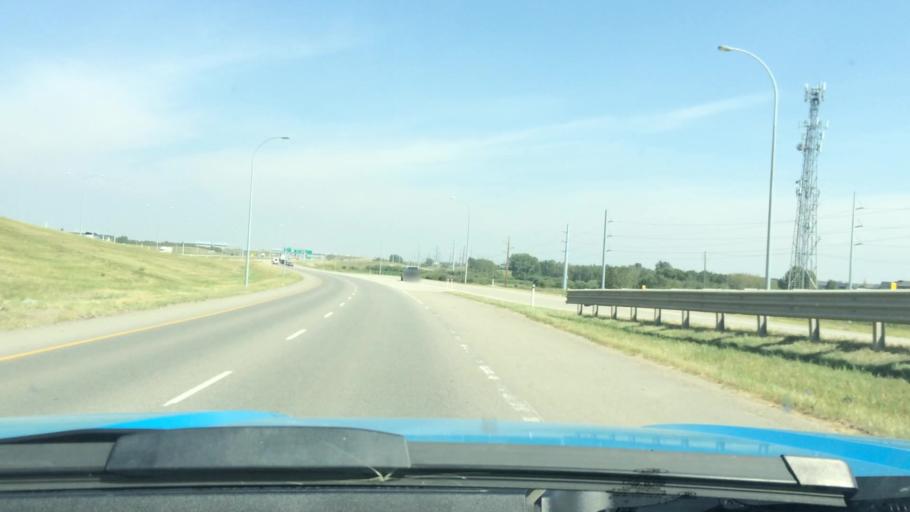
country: CA
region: Alberta
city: Okotoks
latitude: 50.9006
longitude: -113.9688
